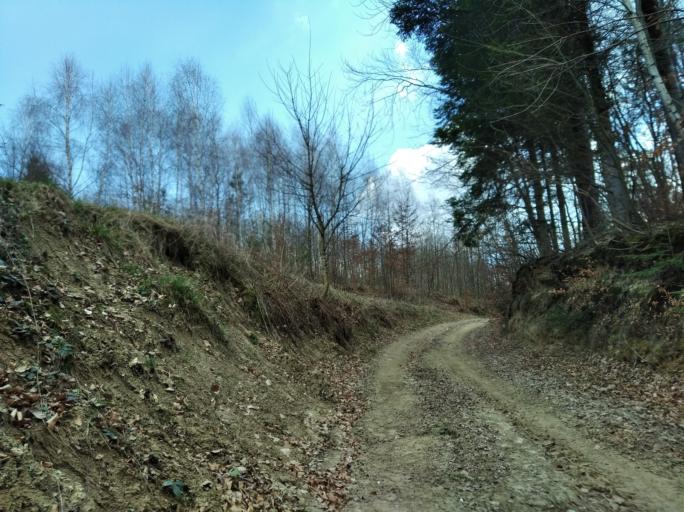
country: PL
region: Subcarpathian Voivodeship
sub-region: Powiat strzyzowski
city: Jawornik
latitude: 49.8453
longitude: 21.8490
